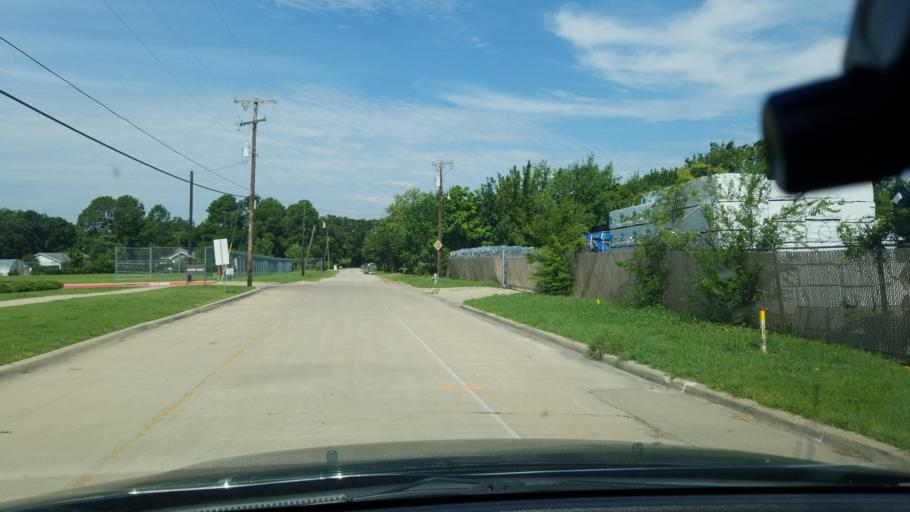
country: US
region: Texas
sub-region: Dallas County
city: Balch Springs
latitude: 32.7288
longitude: -96.6245
